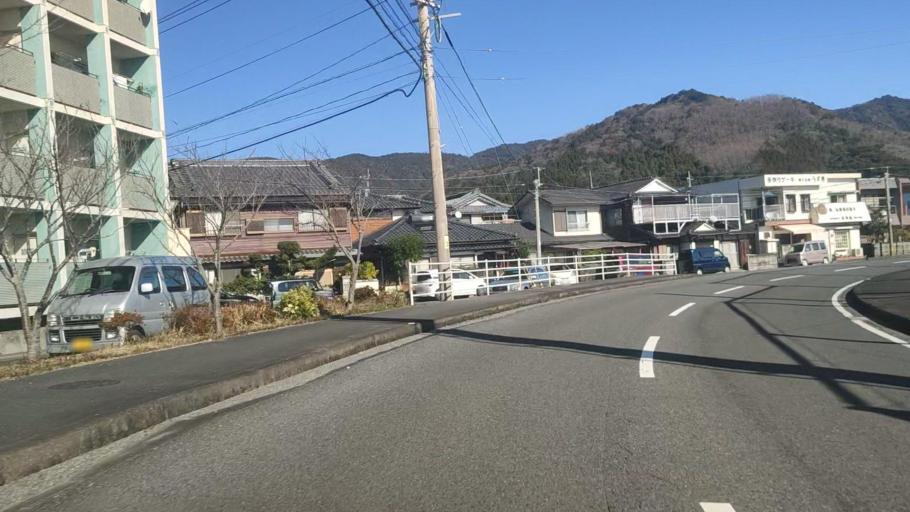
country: JP
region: Oita
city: Saiki
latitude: 32.8011
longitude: 131.9201
